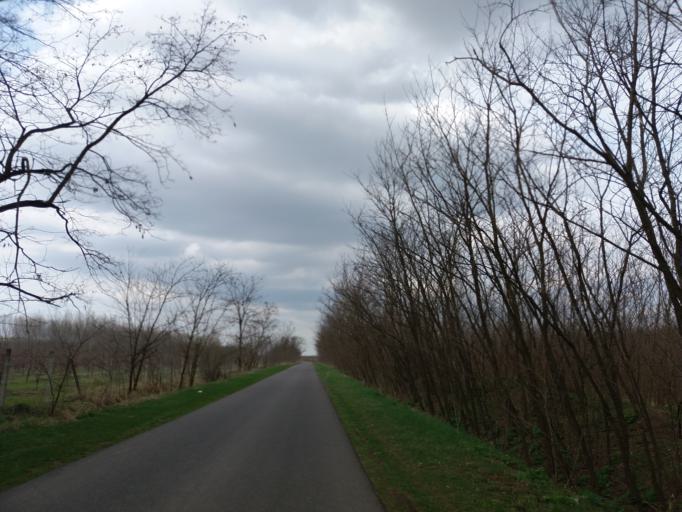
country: HU
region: Szabolcs-Szatmar-Bereg
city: Nyirtass
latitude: 48.0831
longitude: 22.0388
